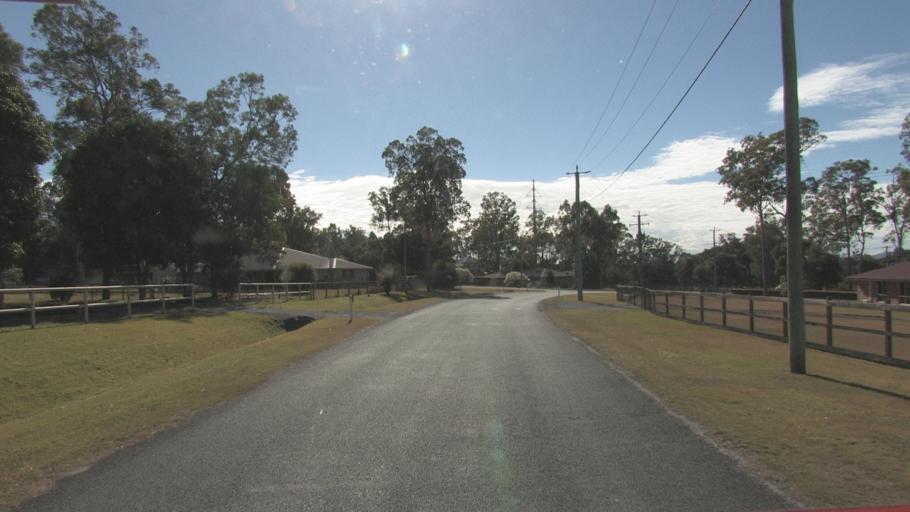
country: AU
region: Queensland
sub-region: Logan
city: Chambers Flat
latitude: -27.7746
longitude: 153.0784
